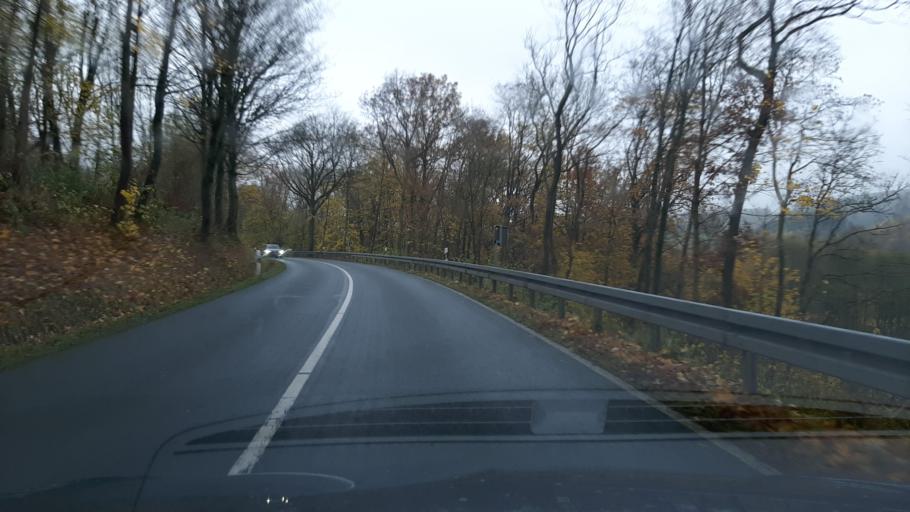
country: DE
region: North Rhine-Westphalia
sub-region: Regierungsbezirk Arnsberg
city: Winterberg
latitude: 51.2625
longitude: 8.4715
